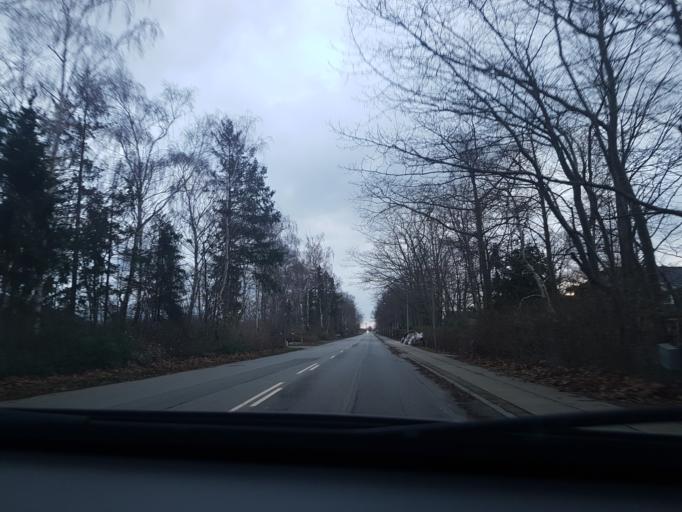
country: DK
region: Capital Region
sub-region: Ishoj Kommune
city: Ishoj
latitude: 55.6115
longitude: 12.3679
